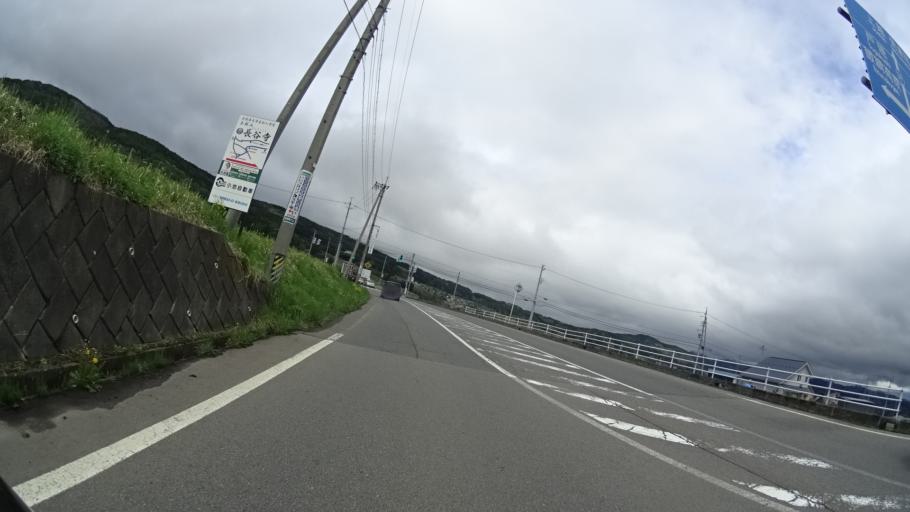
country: JP
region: Nagano
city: Nagano-shi
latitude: 36.7323
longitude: 138.2084
